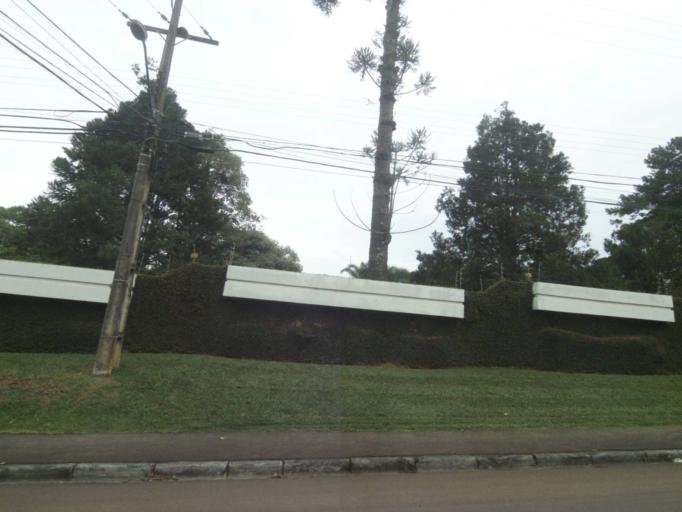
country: BR
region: Parana
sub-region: Curitiba
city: Curitiba
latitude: -25.4531
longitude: -49.3308
